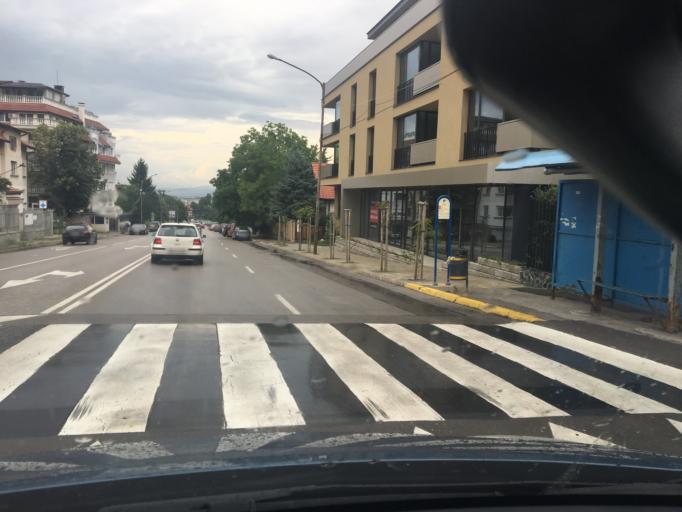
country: BG
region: Sofia-Capital
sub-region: Stolichna Obshtina
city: Sofia
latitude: 42.6555
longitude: 23.2656
